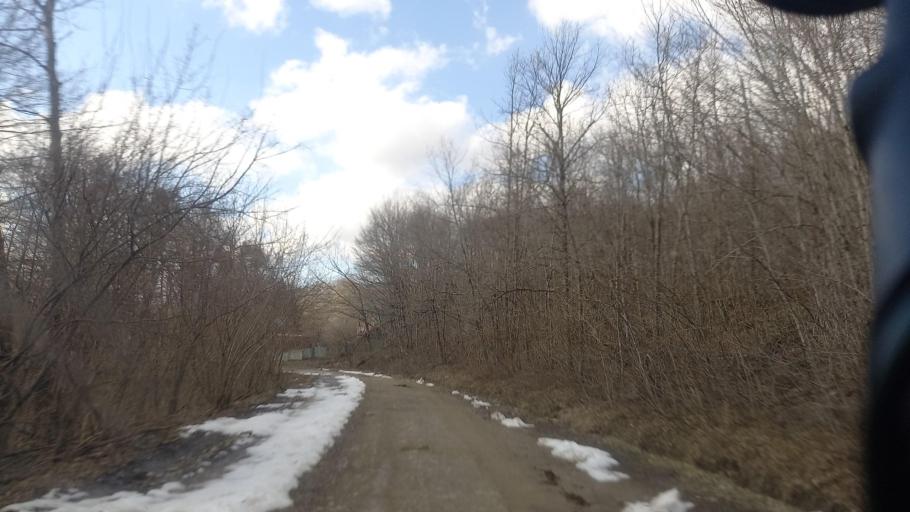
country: RU
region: Krasnodarskiy
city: Smolenskaya
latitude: 44.6016
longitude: 38.8742
